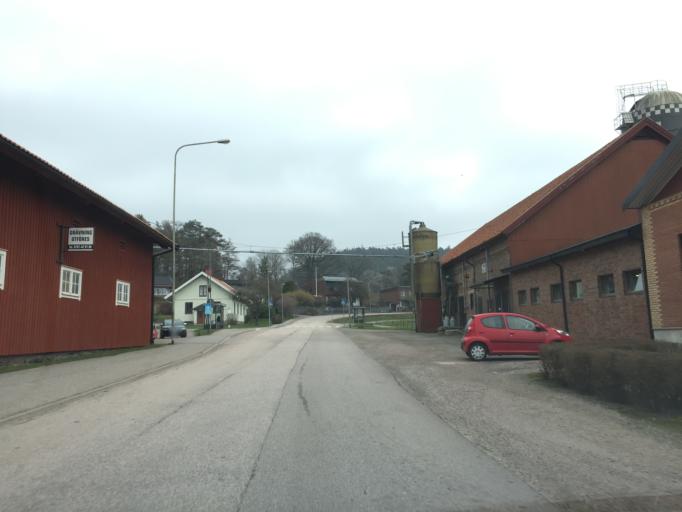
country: SE
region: Vaestra Goetaland
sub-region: Partille Kommun
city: Furulund
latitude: 57.7484
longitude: 12.1459
